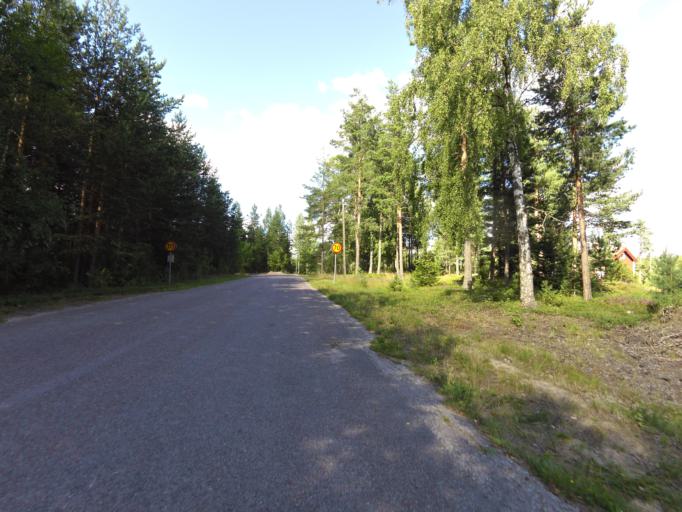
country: SE
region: Dalarna
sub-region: Faluns Kommun
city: Svardsjo
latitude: 60.6623
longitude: 15.8416
